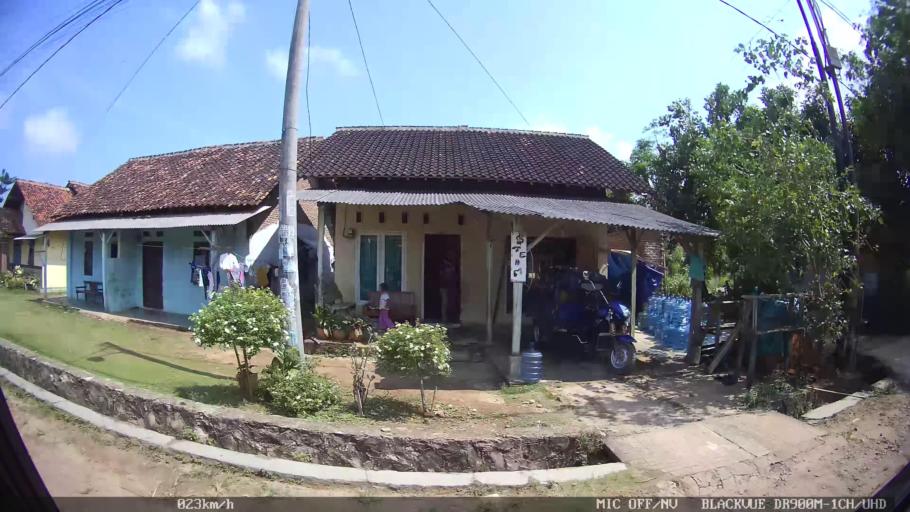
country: ID
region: Lampung
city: Kedaton
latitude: -5.3451
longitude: 105.2913
